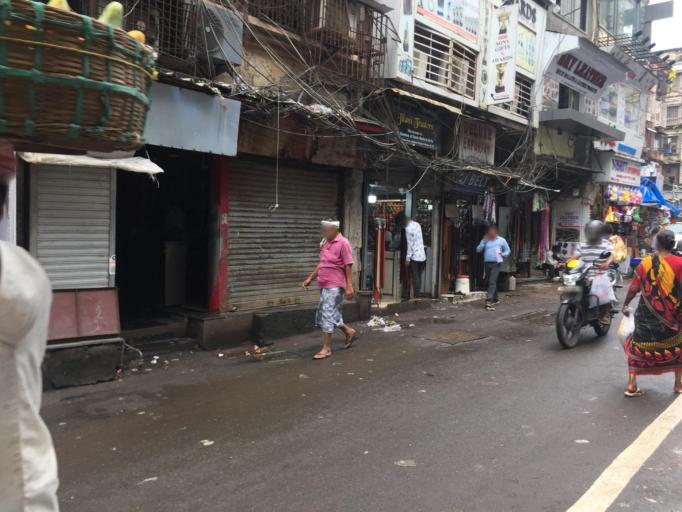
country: IN
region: Maharashtra
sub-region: Raigarh
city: Uran
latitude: 18.9486
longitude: 72.8336
